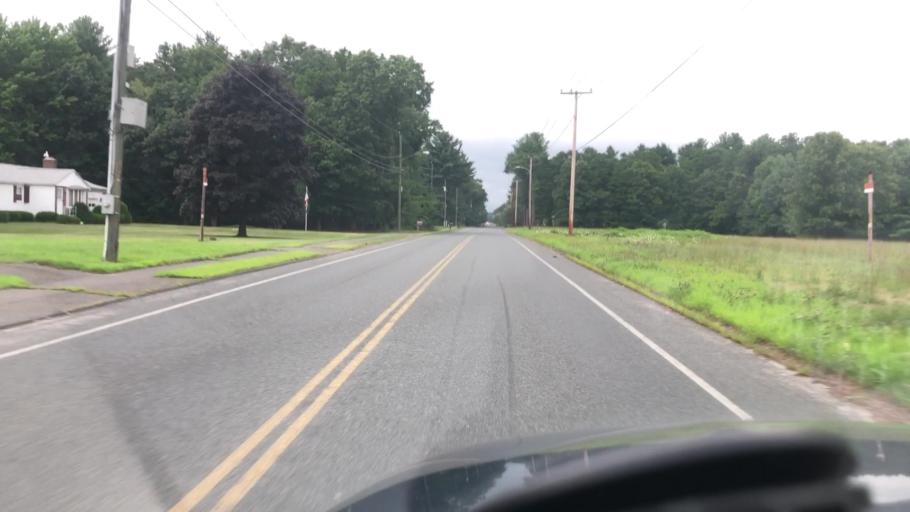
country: US
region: Massachusetts
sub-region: Hampshire County
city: Southampton
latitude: 42.1942
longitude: -72.6871
